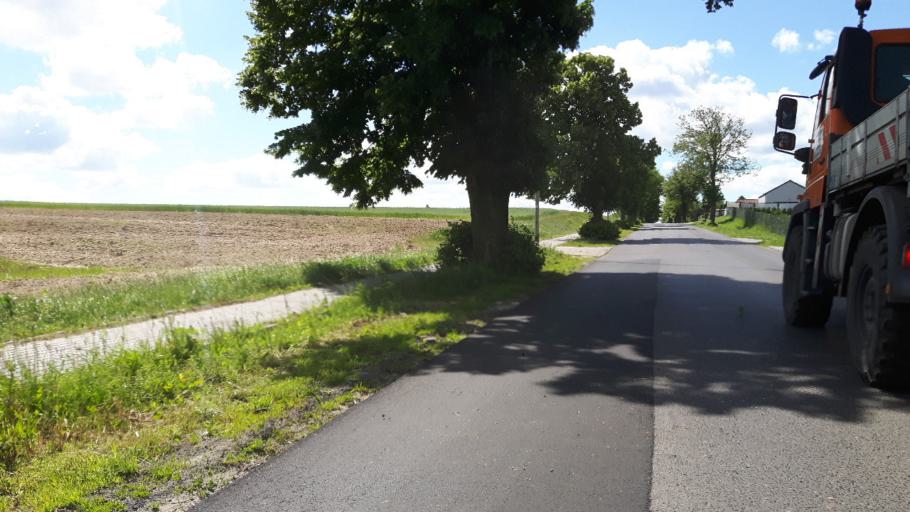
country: PL
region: Pomeranian Voivodeship
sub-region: Powiat pucki
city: Mosty
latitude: 54.6027
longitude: 18.4978
